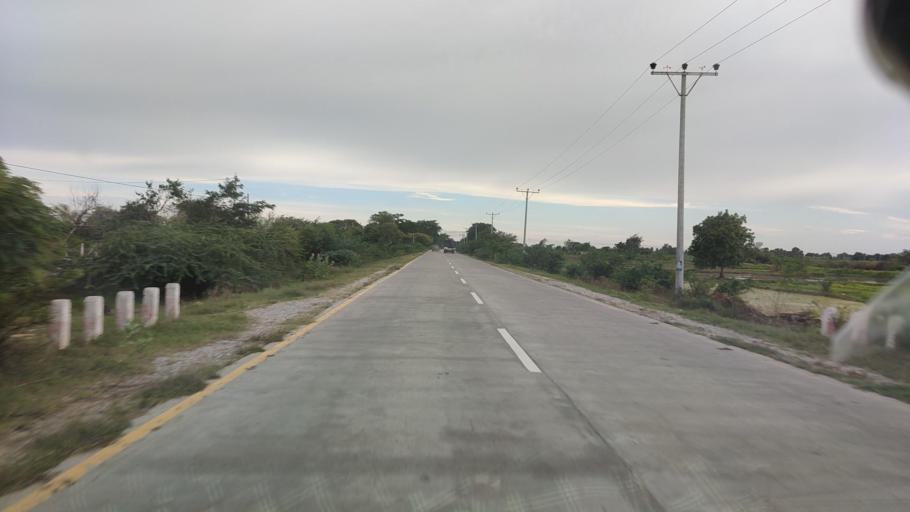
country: MM
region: Mandalay
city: Kyaukse
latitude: 21.3160
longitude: 96.0213
